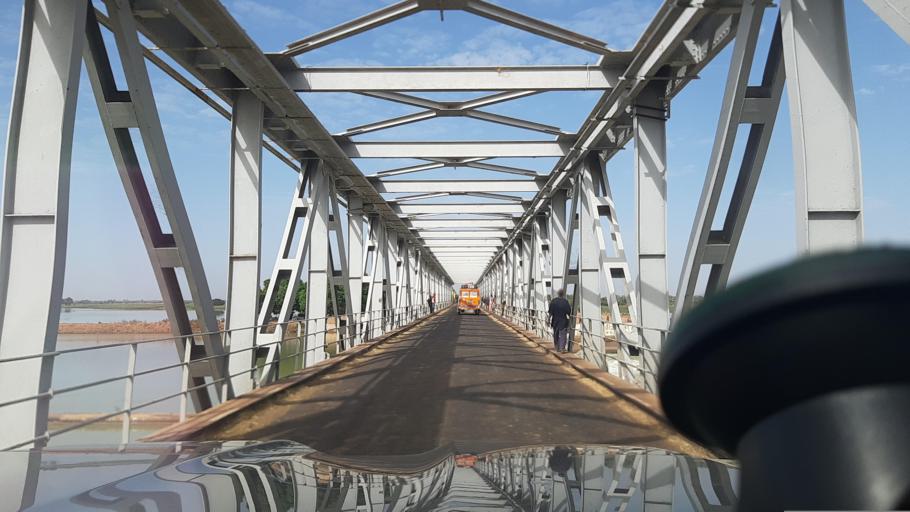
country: ML
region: Segou
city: Markala
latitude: 13.6800
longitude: -6.0811
